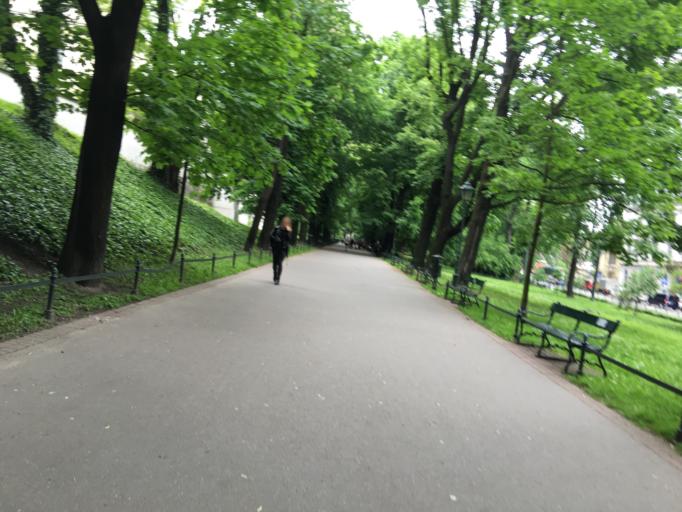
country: PL
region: Lesser Poland Voivodeship
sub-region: Krakow
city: Krakow
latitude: 50.0575
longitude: 19.9402
